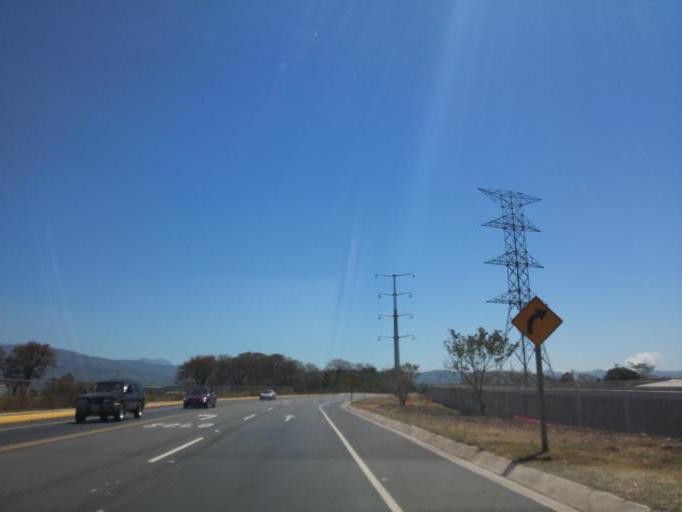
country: CR
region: Alajuela
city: Carrillos
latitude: 9.9924
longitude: -84.2690
